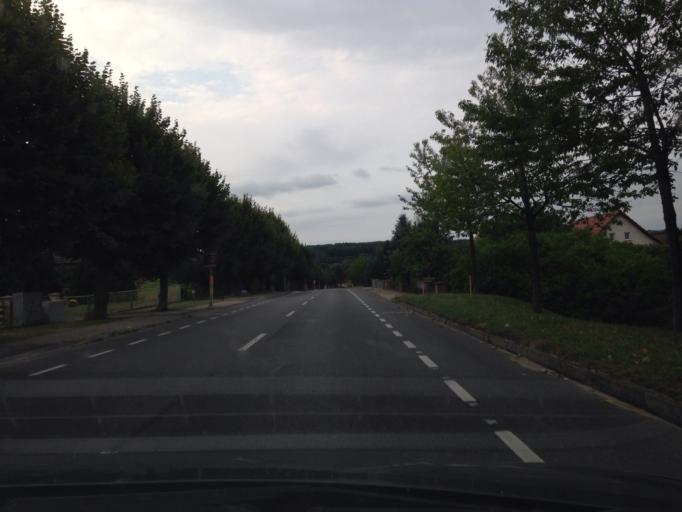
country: DE
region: Mecklenburg-Vorpommern
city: Loitz
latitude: 53.3330
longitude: 13.4302
